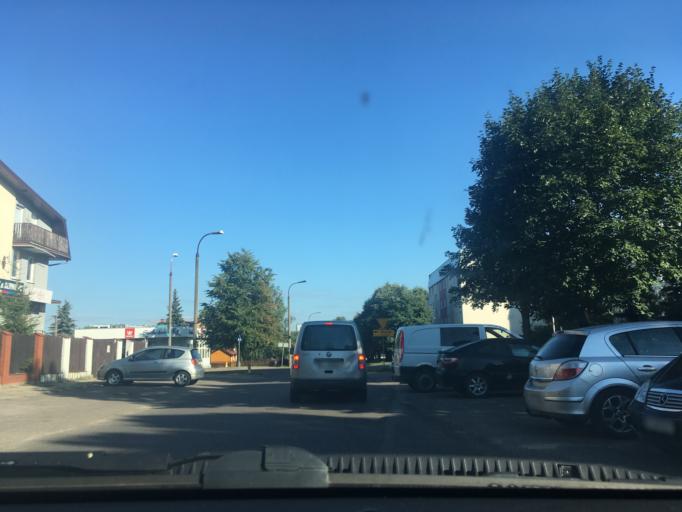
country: PL
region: Podlasie
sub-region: Bialystok
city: Bialystok
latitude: 53.1422
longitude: 23.1505
